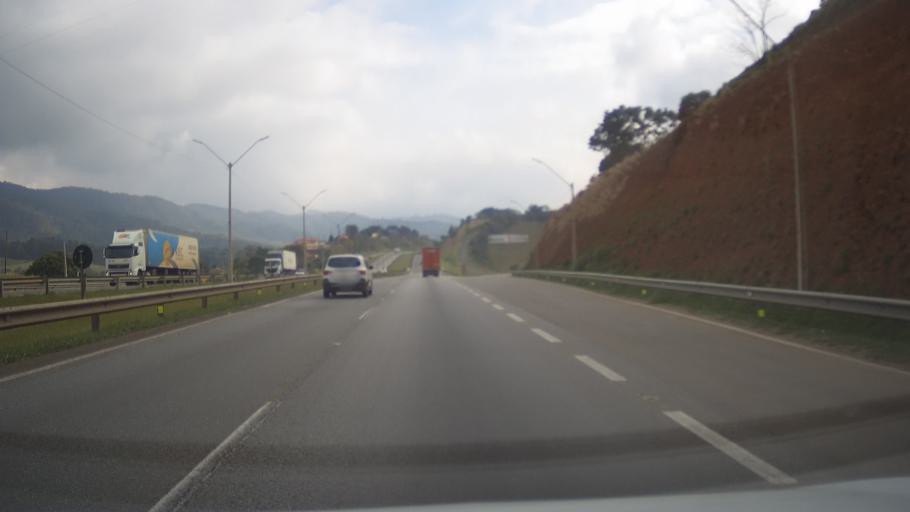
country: BR
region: Minas Gerais
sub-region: Extrema
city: Extrema
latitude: -22.9008
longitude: -46.4202
